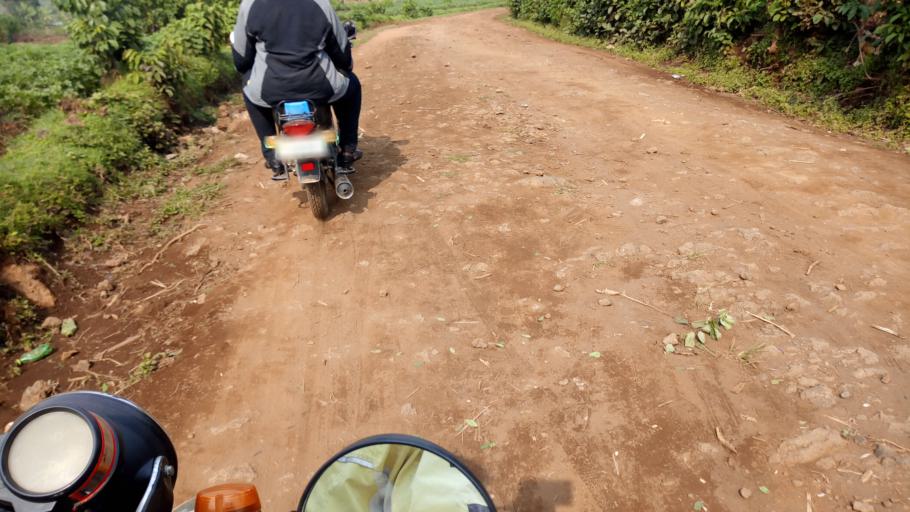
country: UG
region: Western Region
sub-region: Kisoro District
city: Kisoro
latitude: -1.3119
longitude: 29.6532
